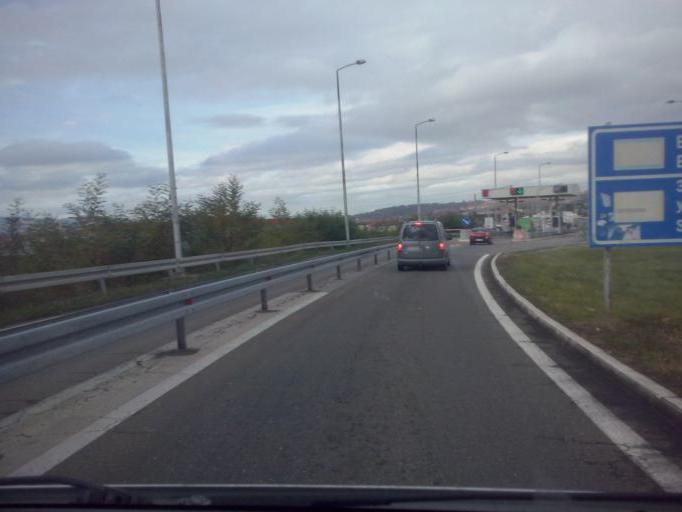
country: RS
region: Central Serbia
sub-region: Pomoravski Okrug
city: Paracin
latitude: 43.8538
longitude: 21.4353
